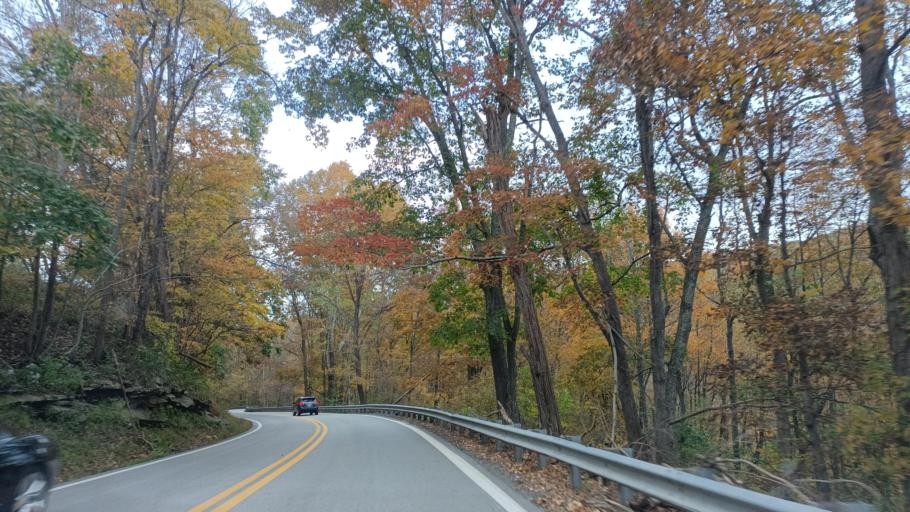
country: US
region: West Virginia
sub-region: Taylor County
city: Grafton
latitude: 39.3333
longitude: -79.9322
